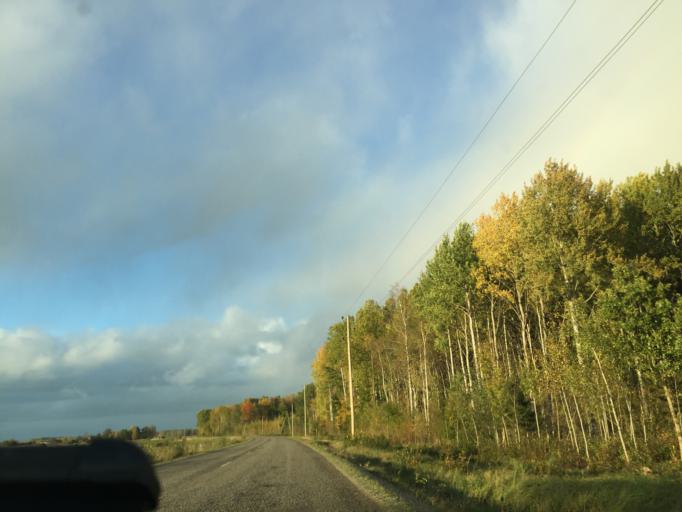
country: LV
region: Broceni
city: Broceni
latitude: 56.8669
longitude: 22.3823
